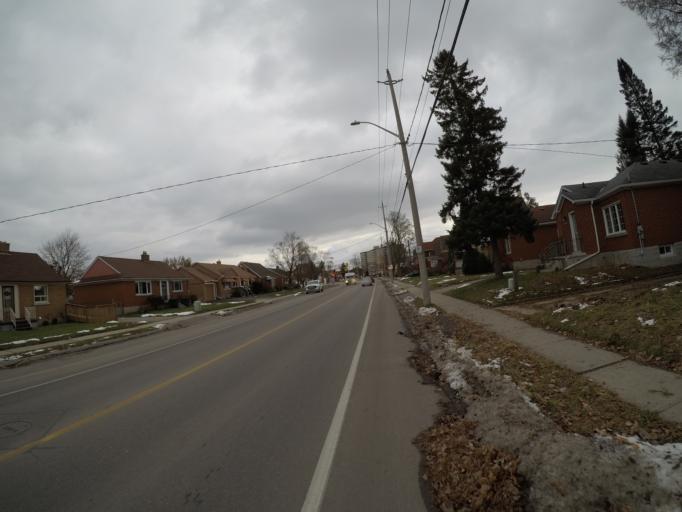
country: CA
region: Ontario
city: Waterloo
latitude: 43.4637
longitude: -80.4950
